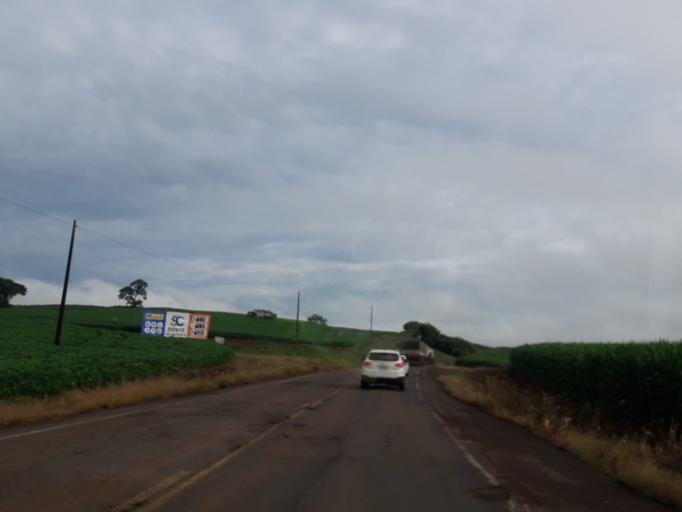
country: AR
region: Misiones
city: Bernardo de Irigoyen
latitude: -26.3423
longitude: -53.5473
